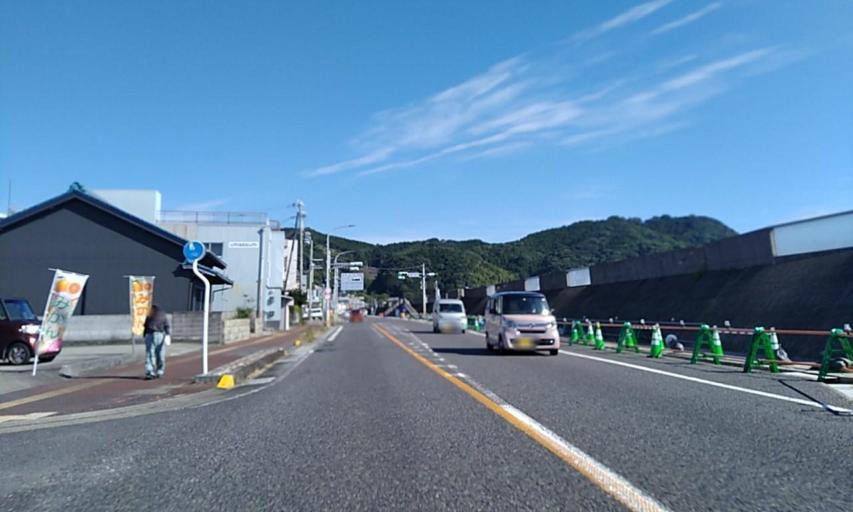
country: JP
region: Wakayama
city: Shingu
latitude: 33.8877
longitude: 136.1020
